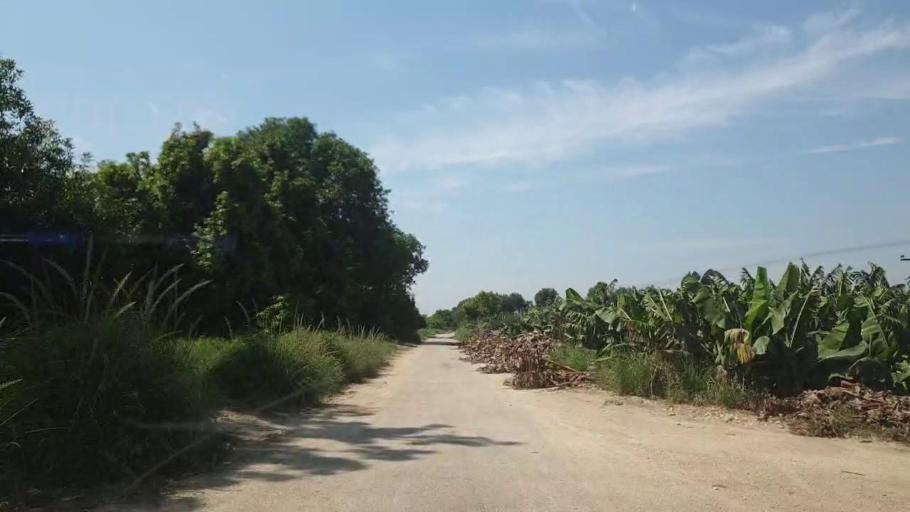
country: PK
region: Sindh
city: Tando Jam
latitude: 25.3991
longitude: 68.6220
